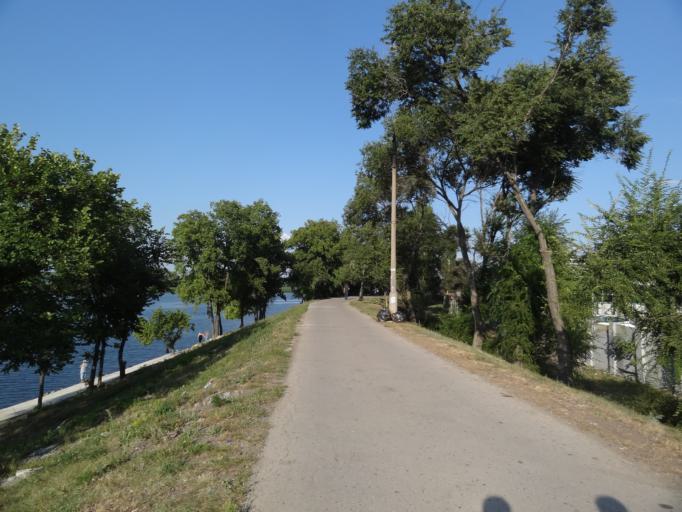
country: RU
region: Saratov
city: Engel's
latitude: 51.5048
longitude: 46.1097
